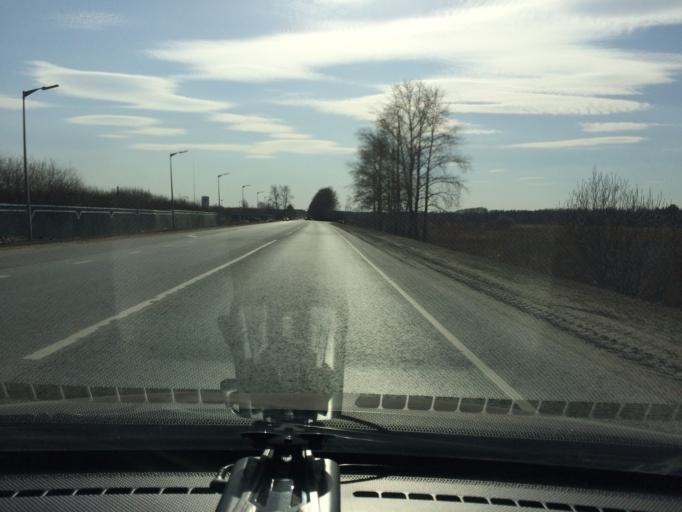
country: RU
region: Mariy-El
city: Yoshkar-Ola
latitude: 56.6547
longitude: 47.9567
